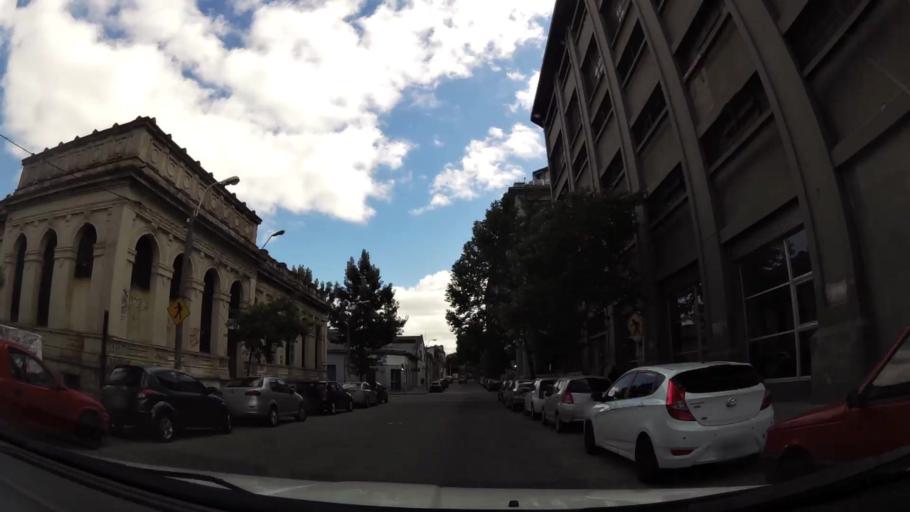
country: UY
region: Montevideo
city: Montevideo
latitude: -34.8885
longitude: -56.1850
